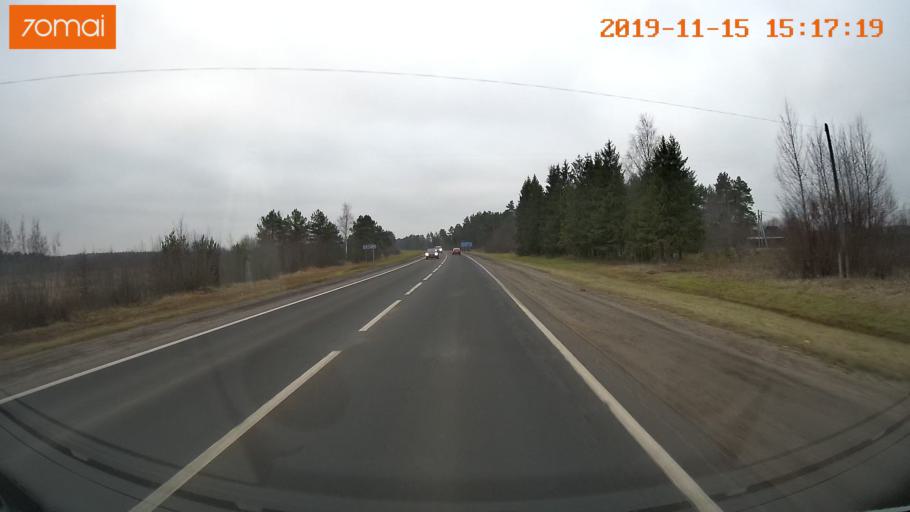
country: RU
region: Jaroslavl
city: Danilov
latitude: 58.2627
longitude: 40.1824
